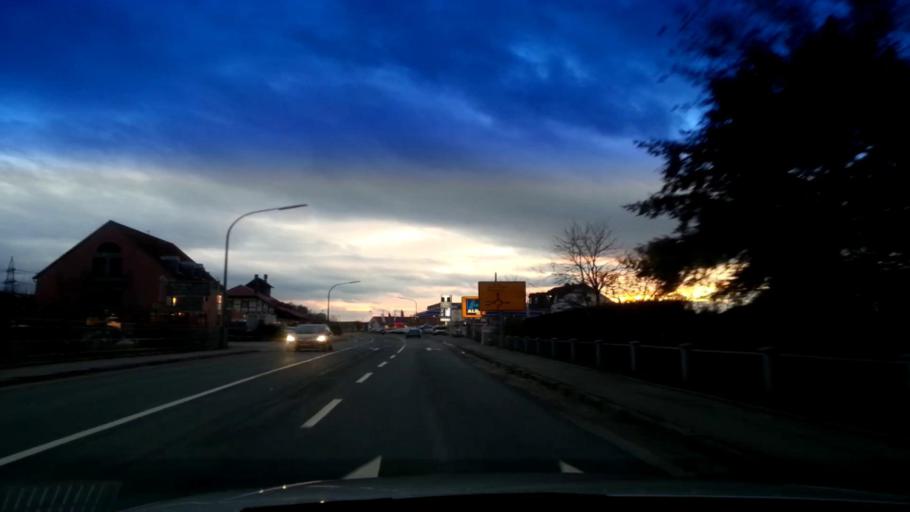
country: DE
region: Bavaria
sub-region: Upper Franconia
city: Schesslitz
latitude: 49.9715
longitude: 11.0267
